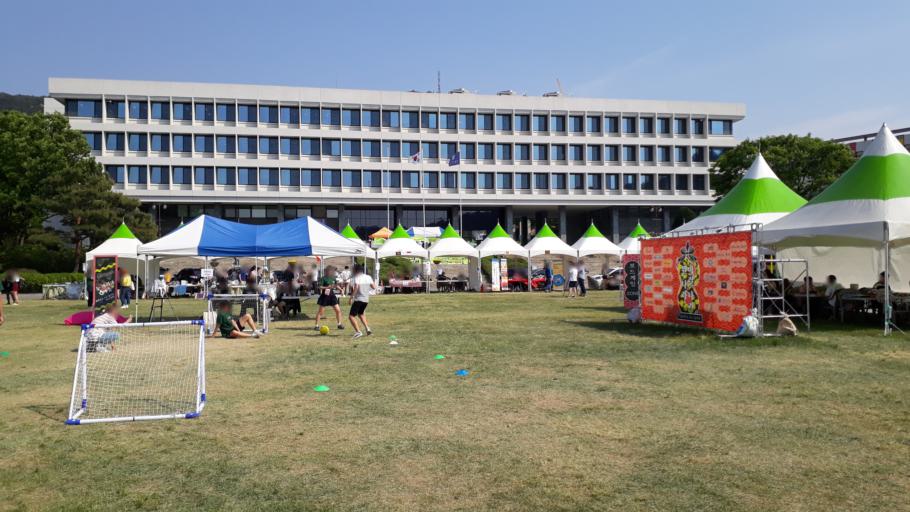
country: KR
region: Gyeonggi-do
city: Anyang-si
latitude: 37.4625
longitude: 126.9492
